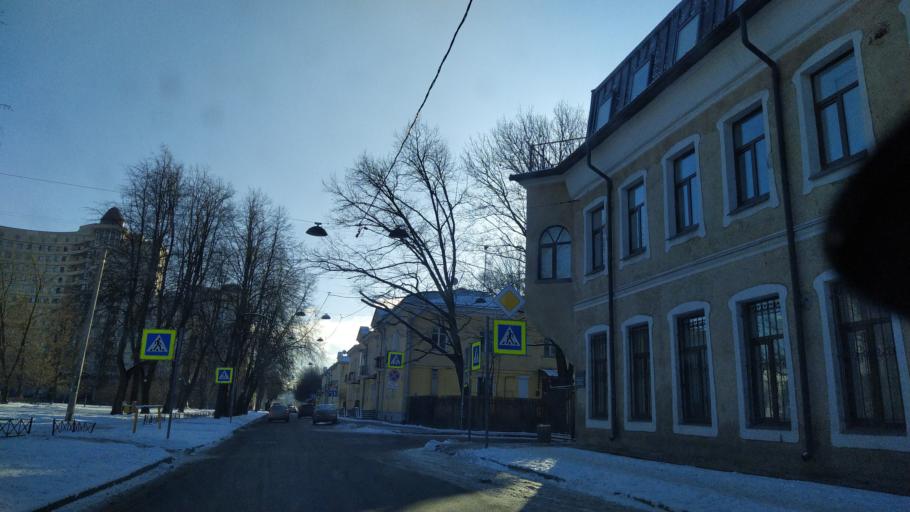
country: RU
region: St.-Petersburg
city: Novaya Derevnya
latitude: 59.9867
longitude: 30.2843
